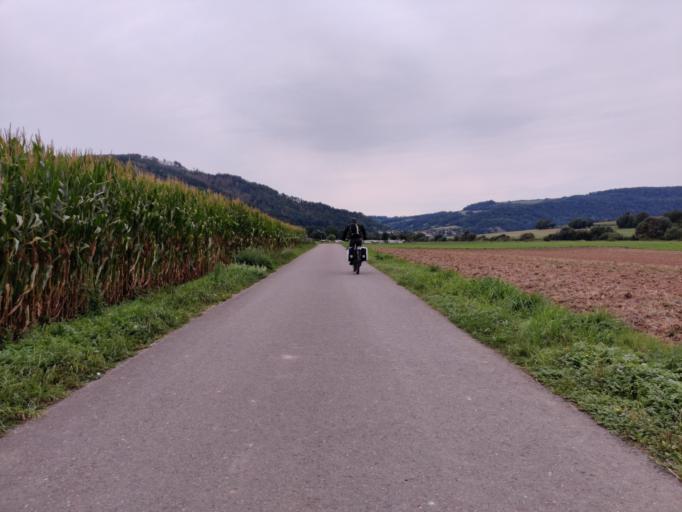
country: DE
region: Lower Saxony
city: Pegestorf
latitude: 51.9479
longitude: 9.5069
